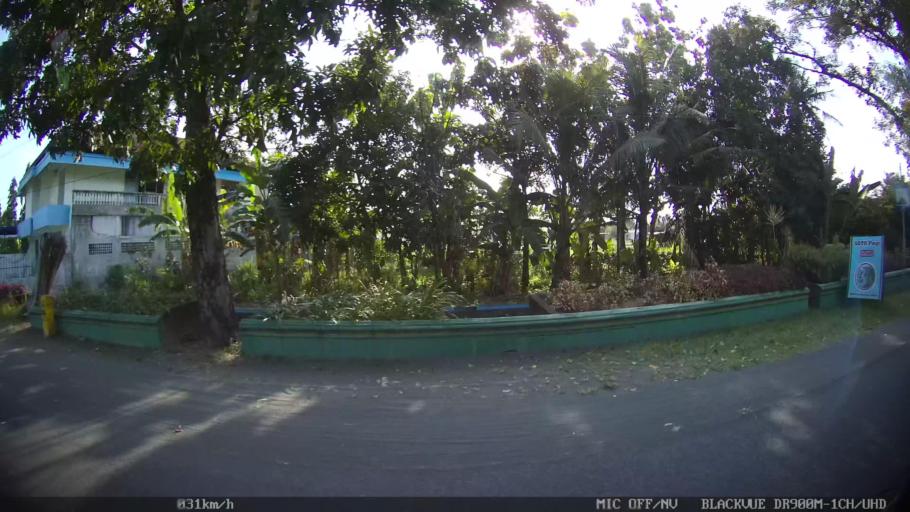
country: ID
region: Daerah Istimewa Yogyakarta
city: Bantul
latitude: -7.9010
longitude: 110.3217
